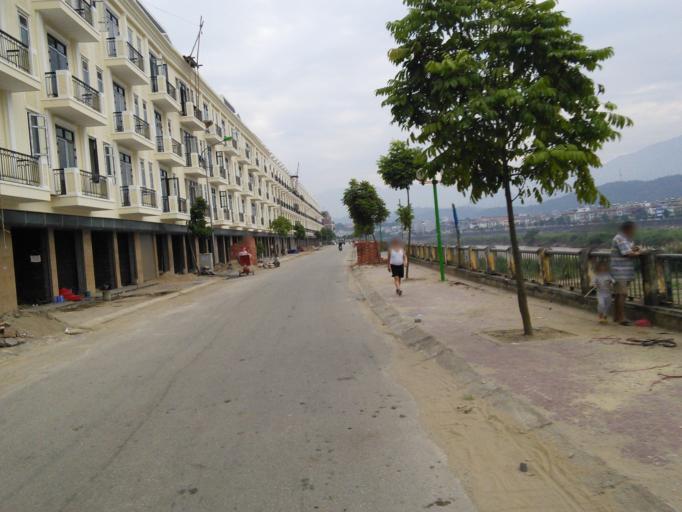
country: VN
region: Lao Cai
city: Lao Cai
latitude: 22.4936
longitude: 103.9737
